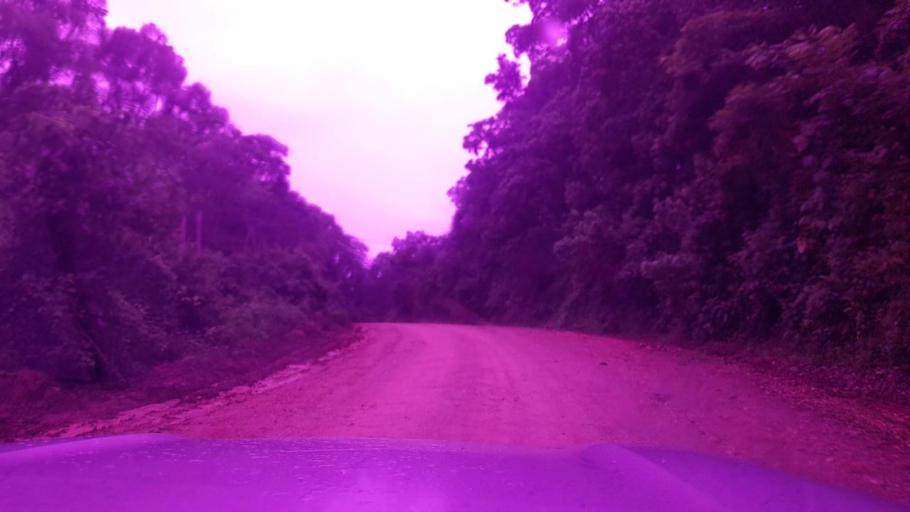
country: ET
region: Southern Nations, Nationalities, and People's Region
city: Bonga
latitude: 7.5046
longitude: 36.0999
